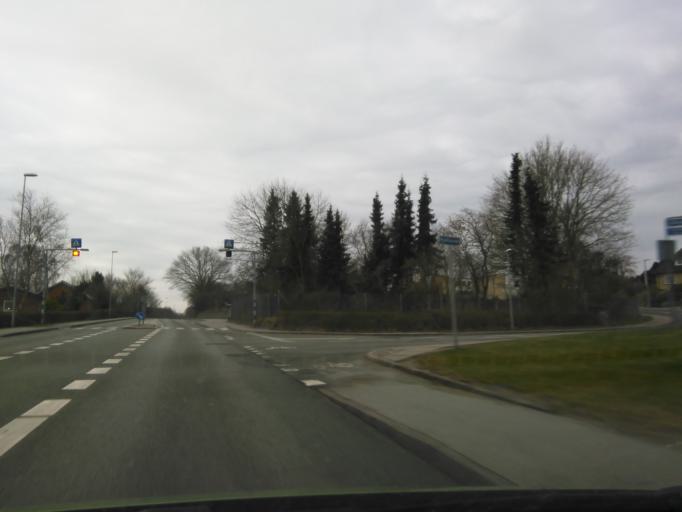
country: DK
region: North Denmark
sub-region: Mariagerfjord Kommune
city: Mariager
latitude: 56.6509
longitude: 9.9760
